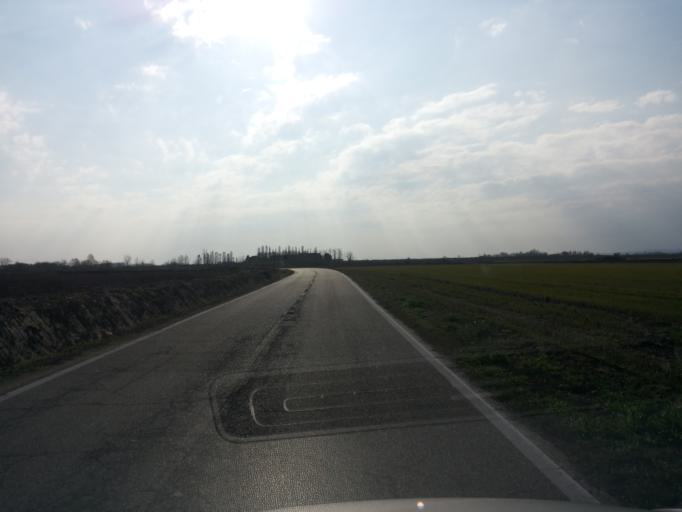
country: IT
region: Piedmont
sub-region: Provincia di Vercelli
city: Pezzana
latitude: 45.2481
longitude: 8.4890
